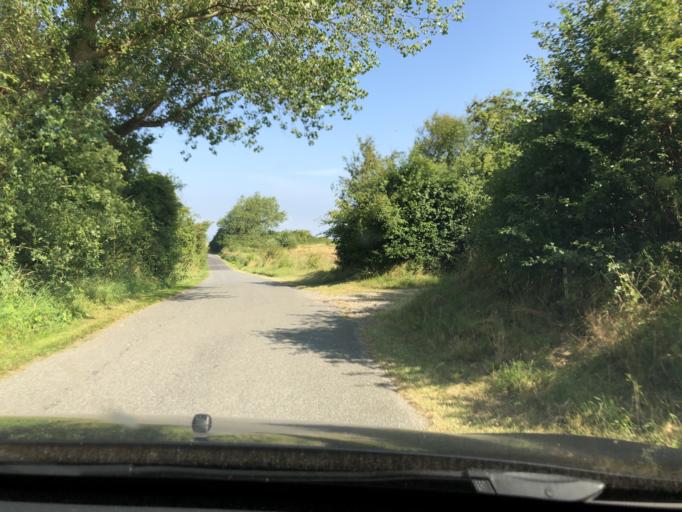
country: DK
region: South Denmark
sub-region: Faaborg-Midtfyn Kommune
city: Faaborg
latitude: 54.9649
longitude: 10.2116
